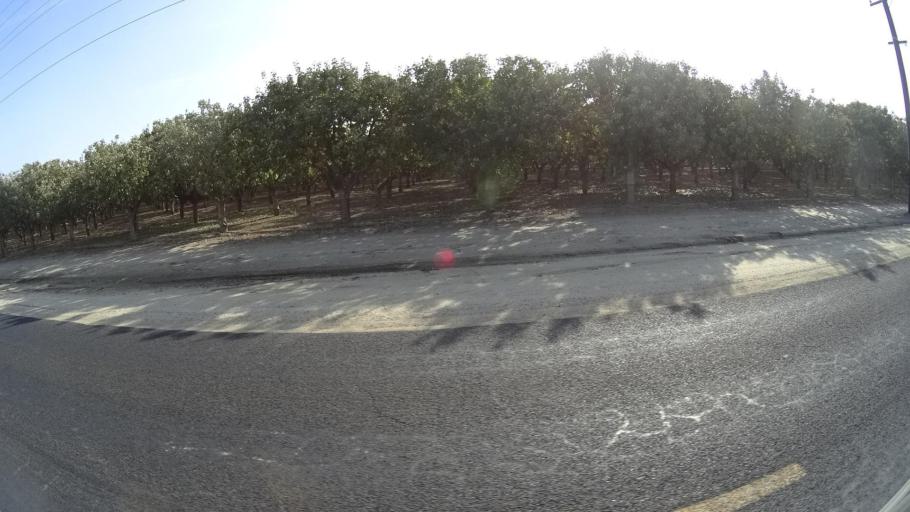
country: US
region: California
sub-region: Kern County
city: Delano
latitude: 35.7759
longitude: -119.2095
